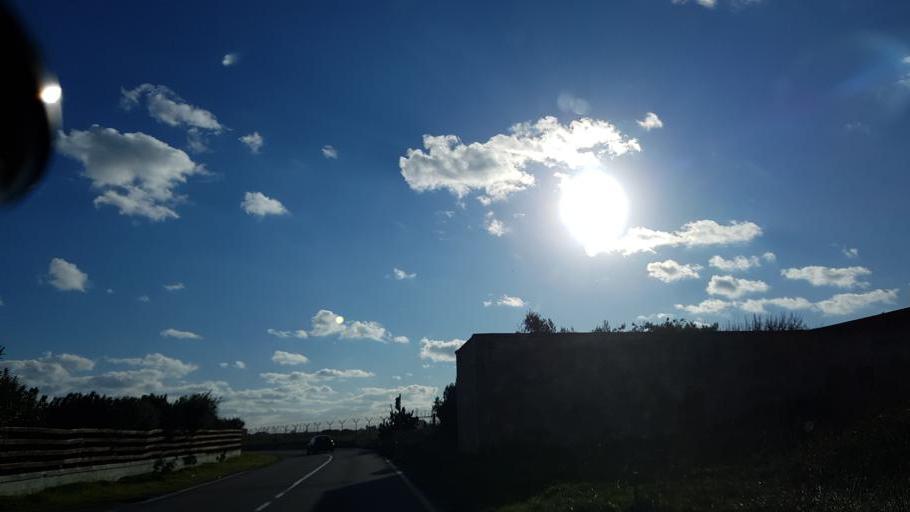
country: IT
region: Apulia
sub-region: Provincia di Brindisi
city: Materdomini
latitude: 40.6641
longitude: 17.9514
